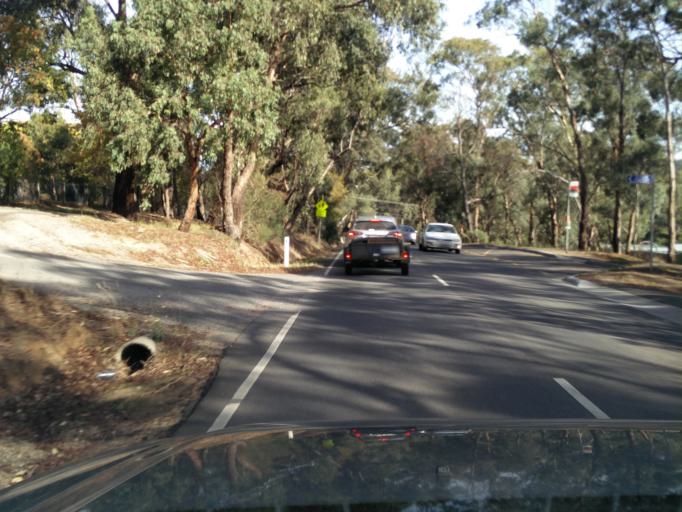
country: AU
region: Victoria
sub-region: Nillumbik
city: Eltham
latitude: -37.7265
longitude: 145.1505
